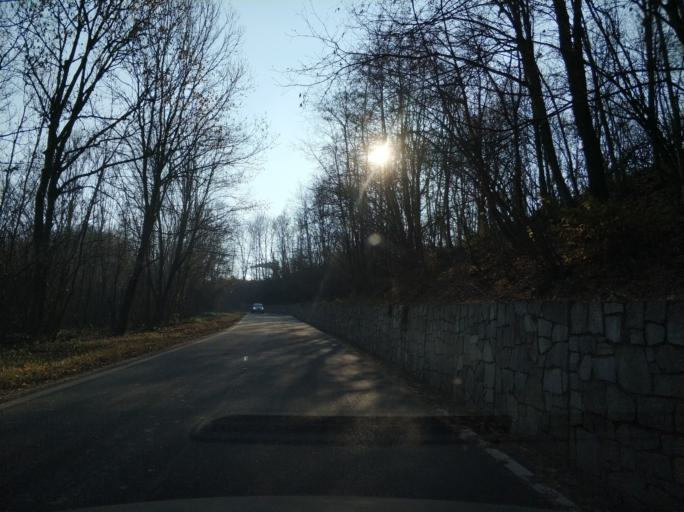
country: IT
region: Piedmont
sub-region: Provincia di Torino
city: Rocca Canavese
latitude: 45.3046
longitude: 7.5776
